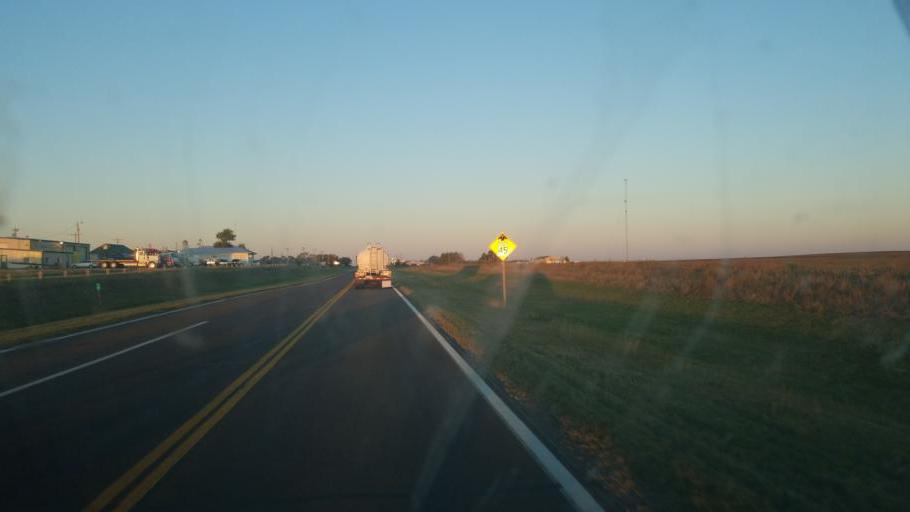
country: US
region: Kansas
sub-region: Wallace County
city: Sharon Springs
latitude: 38.9019
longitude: -101.7416
